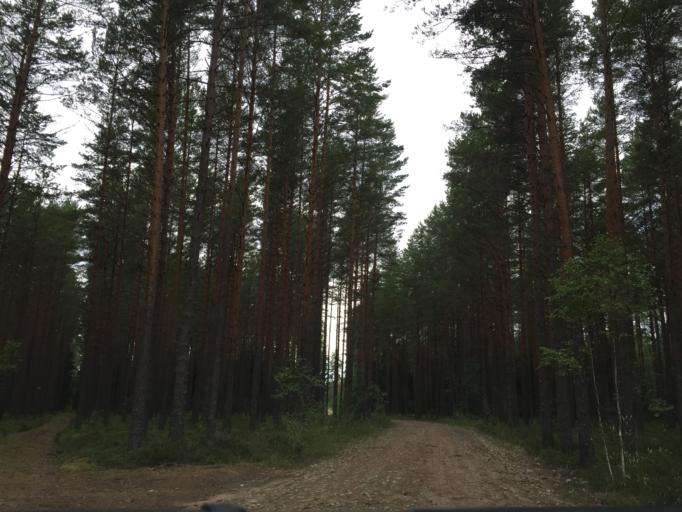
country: LV
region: Saulkrastu
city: Saulkrasti
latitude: 57.2140
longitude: 24.4395
